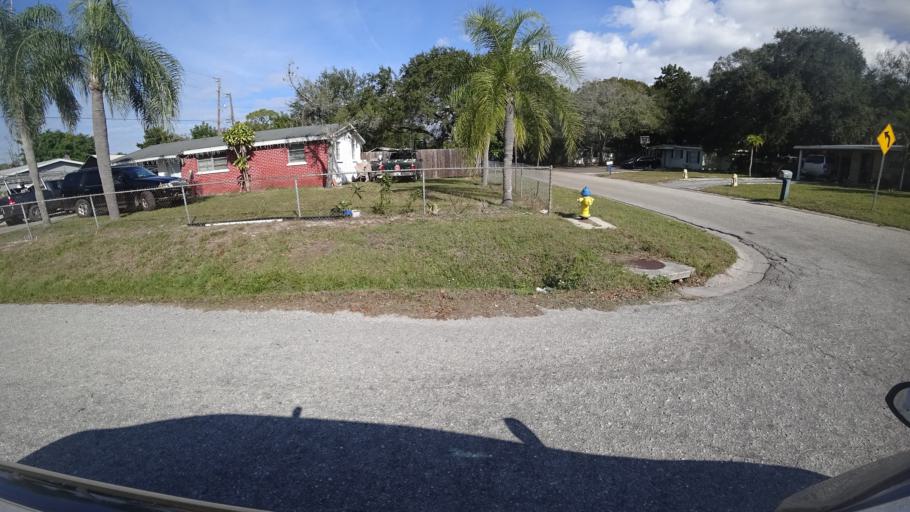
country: US
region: Florida
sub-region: Manatee County
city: Whitfield
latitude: 27.4356
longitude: -82.5637
